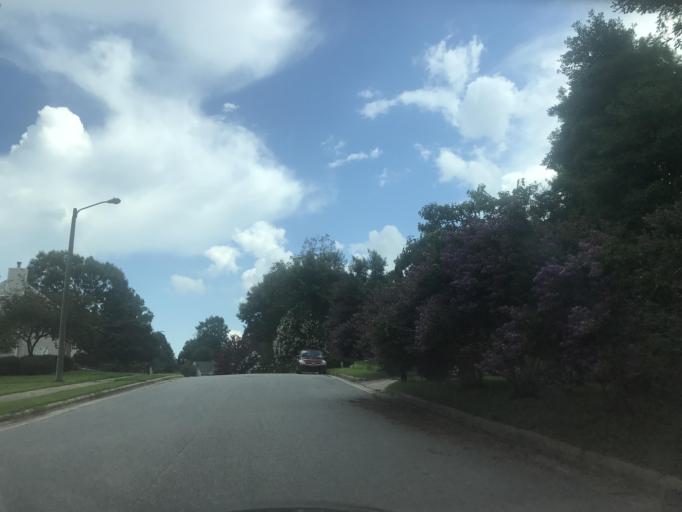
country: US
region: North Carolina
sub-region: Wake County
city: Knightdale
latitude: 35.8354
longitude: -78.5629
